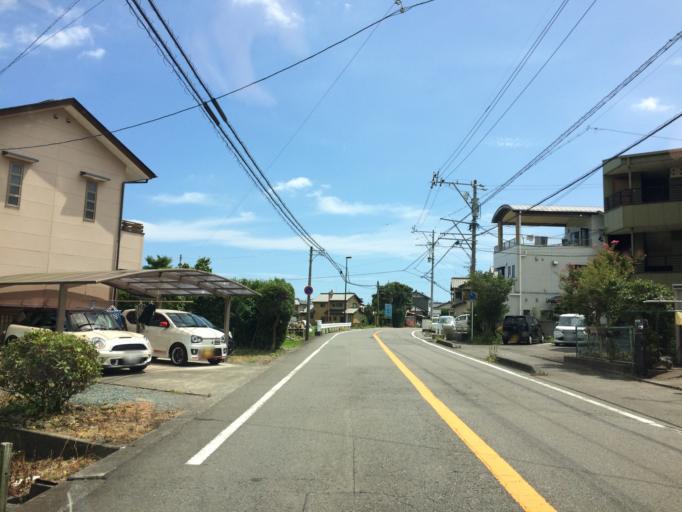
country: JP
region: Shizuoka
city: Yaizu
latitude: 34.8859
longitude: 138.3129
